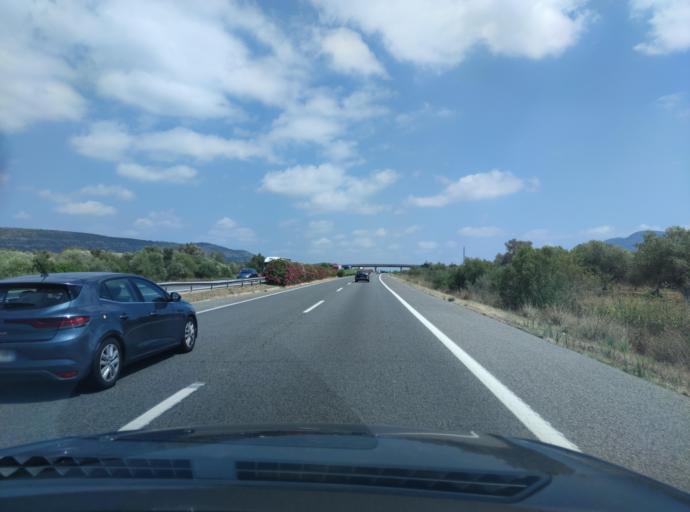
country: ES
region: Catalonia
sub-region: Provincia de Tarragona
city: Ulldecona
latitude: 40.6107
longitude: 0.4771
